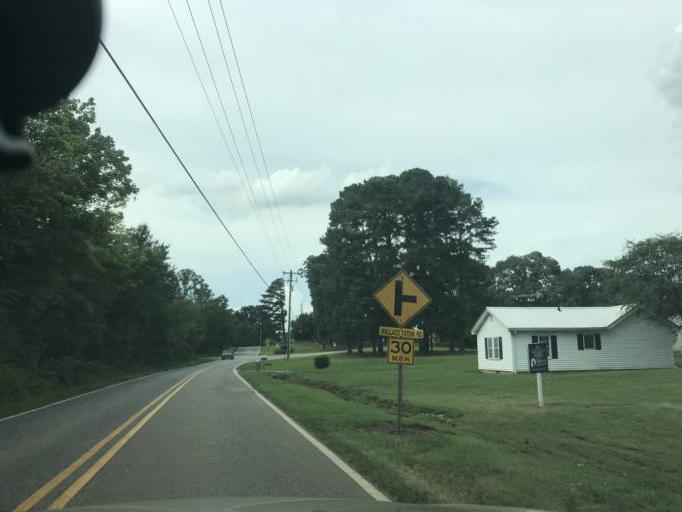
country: US
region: Georgia
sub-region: Forsyth County
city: Cumming
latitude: 34.2810
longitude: -84.2362
